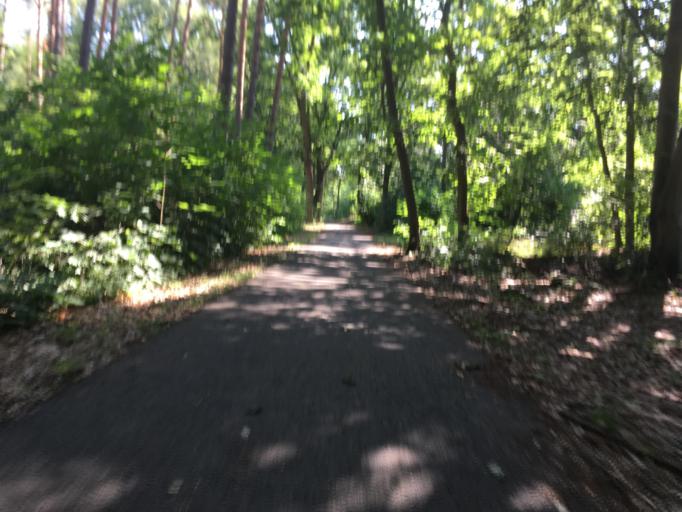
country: DE
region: Brandenburg
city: Templin
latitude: 53.1301
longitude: 13.5435
